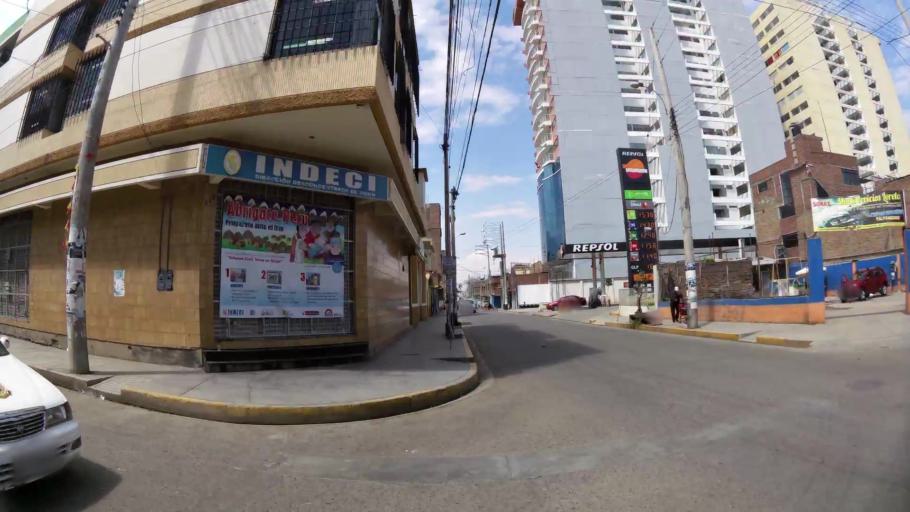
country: PE
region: Junin
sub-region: Provincia de Huancayo
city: El Tambo
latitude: -12.0729
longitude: -75.2143
